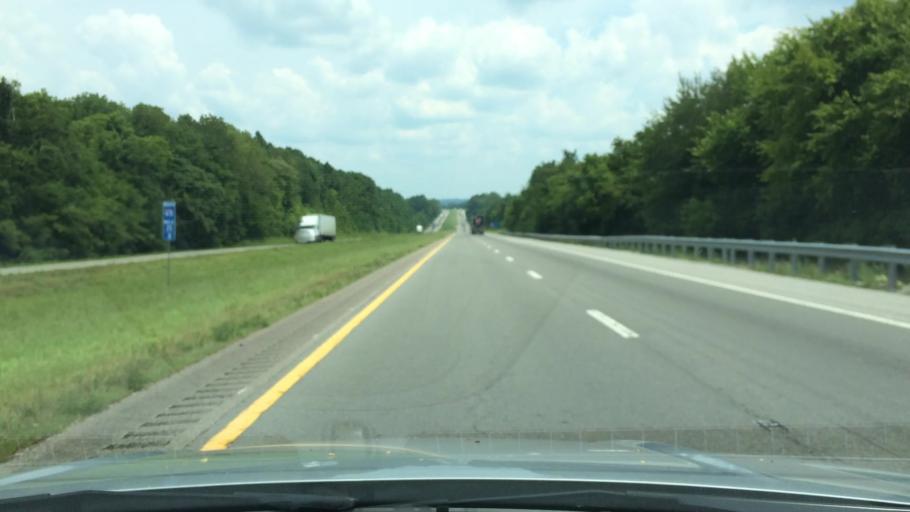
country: US
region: Tennessee
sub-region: Marshall County
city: Cornersville
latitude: 35.2833
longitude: -86.8856
